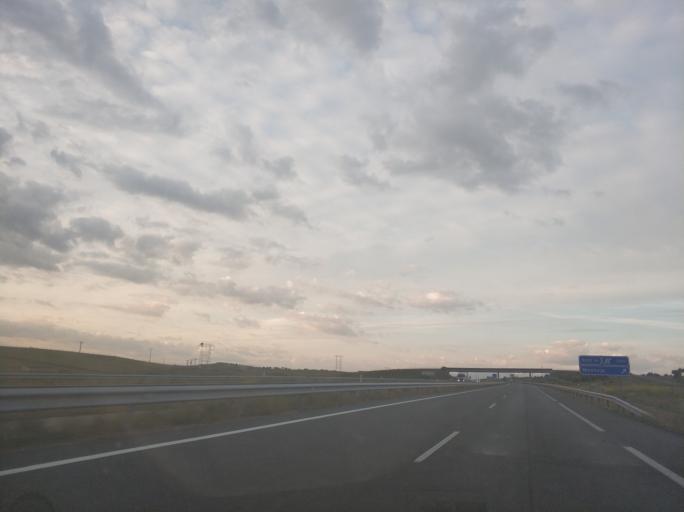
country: ES
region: Castille and Leon
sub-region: Provincia de Salamanca
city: Montejo
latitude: 40.6413
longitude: -5.6310
